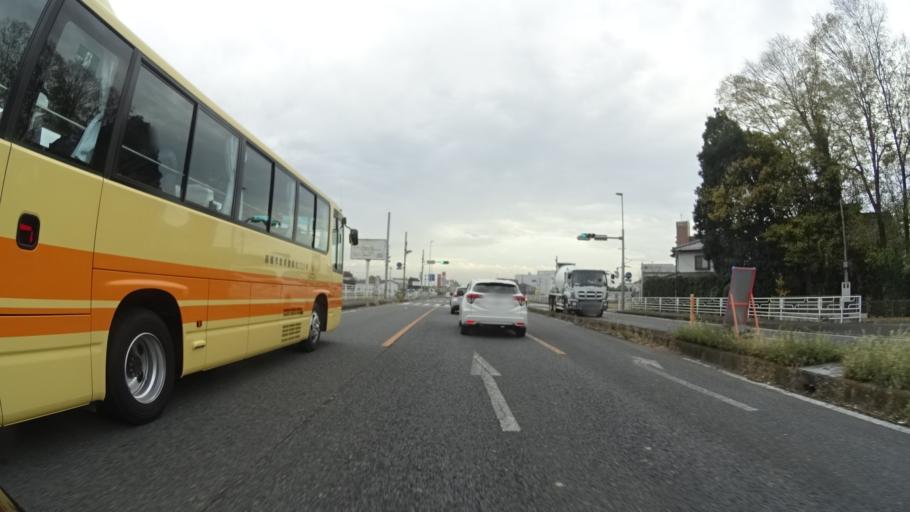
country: JP
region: Gunma
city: Maebashi-shi
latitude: 36.3805
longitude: 139.1071
